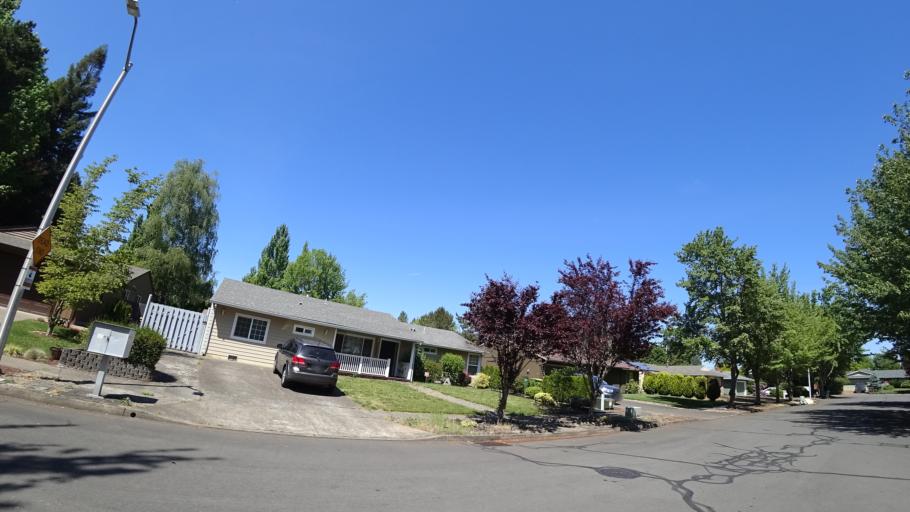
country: US
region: Oregon
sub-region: Washington County
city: Tigard
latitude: 45.4452
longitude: -122.8118
